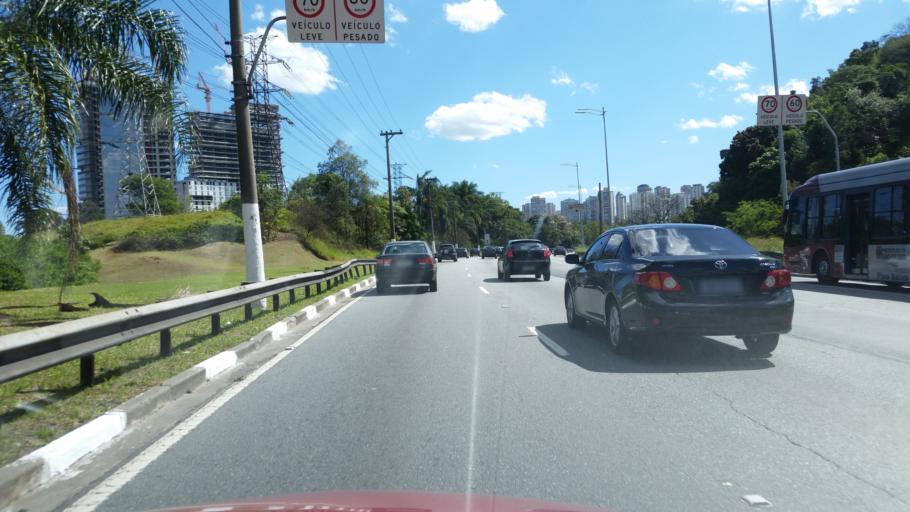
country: BR
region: Sao Paulo
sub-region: Taboao Da Serra
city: Taboao da Serra
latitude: -23.6211
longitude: -46.7035
